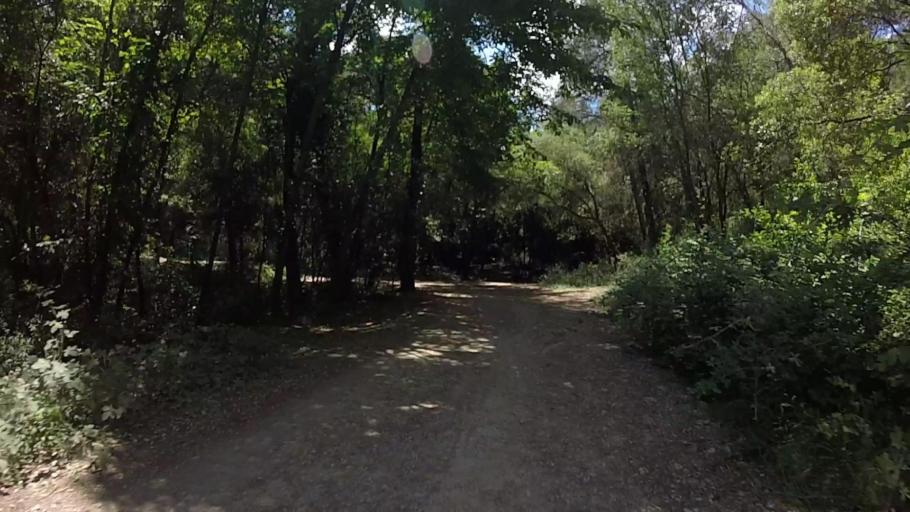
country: FR
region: Provence-Alpes-Cote d'Azur
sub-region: Departement des Alpes-Maritimes
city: Mougins
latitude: 43.5999
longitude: 7.0250
